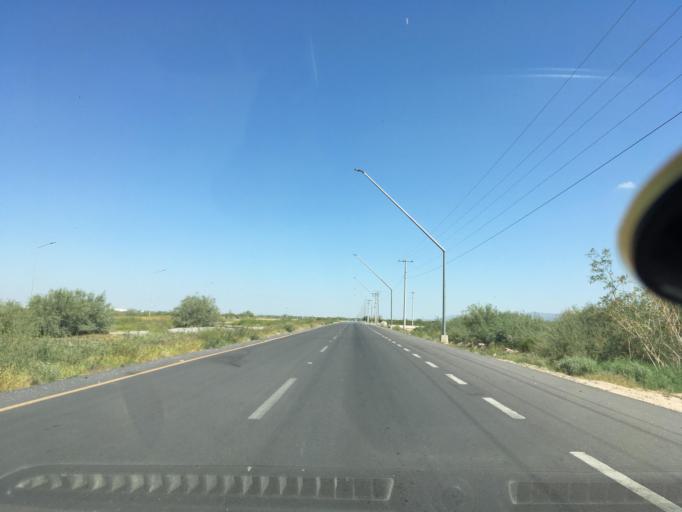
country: MX
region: Coahuila
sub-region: Torreon
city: Fraccionamiento la Noria
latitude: 25.4687
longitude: -103.3221
